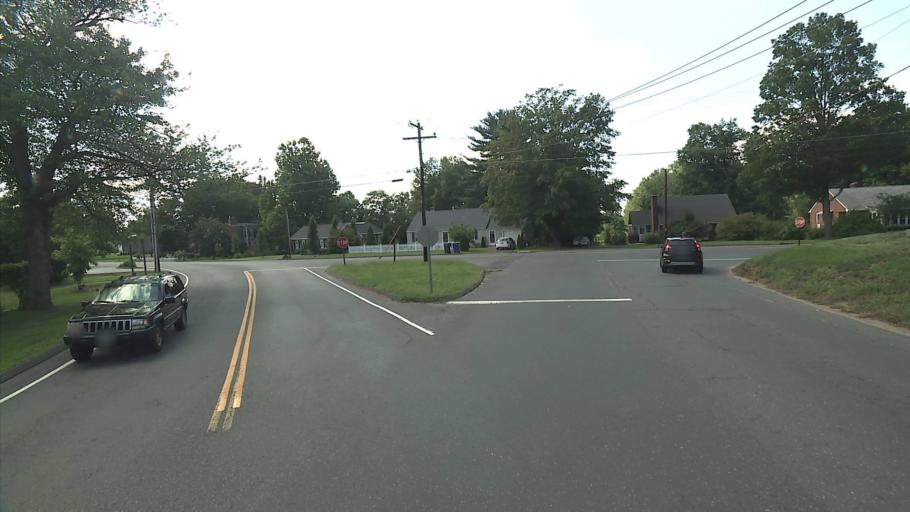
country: US
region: Connecticut
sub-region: Hartford County
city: Suffield Depot
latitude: 41.9990
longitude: -72.6342
